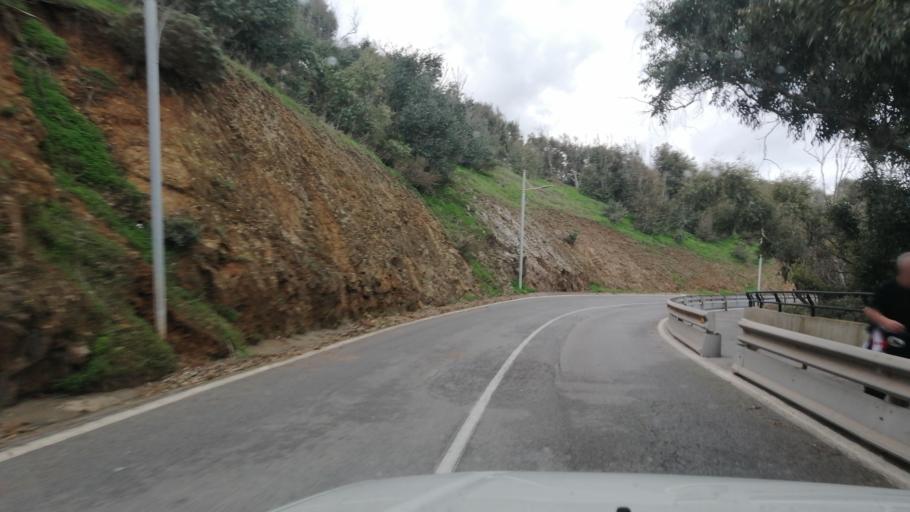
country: ES
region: Ceuta
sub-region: Ceuta
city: Ceuta
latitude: 35.9003
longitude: -5.2844
